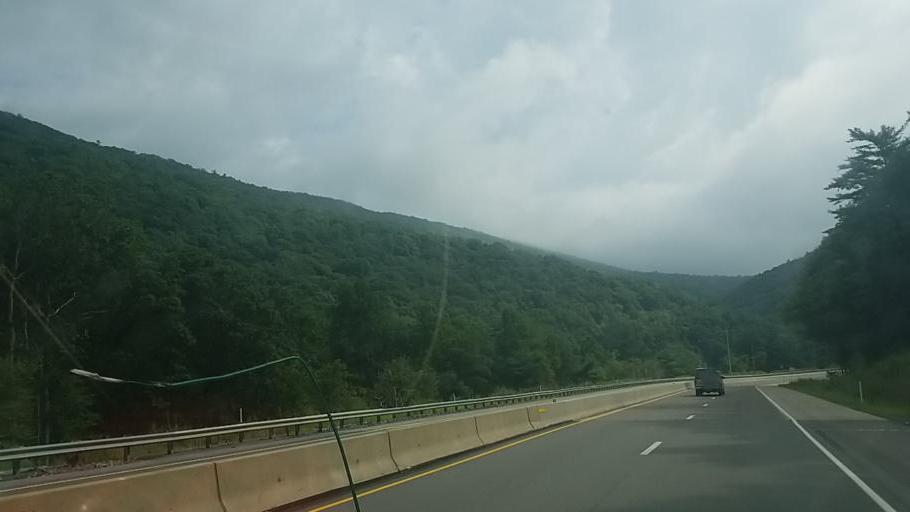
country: US
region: Pennsylvania
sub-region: Mifflin County
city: Milroy
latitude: 40.7302
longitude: -77.6186
